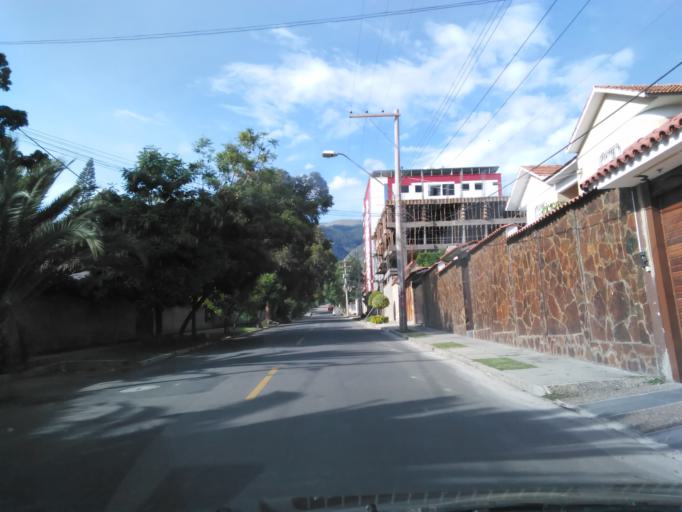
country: BO
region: Cochabamba
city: Cochabamba
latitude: -17.3700
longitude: -66.1461
